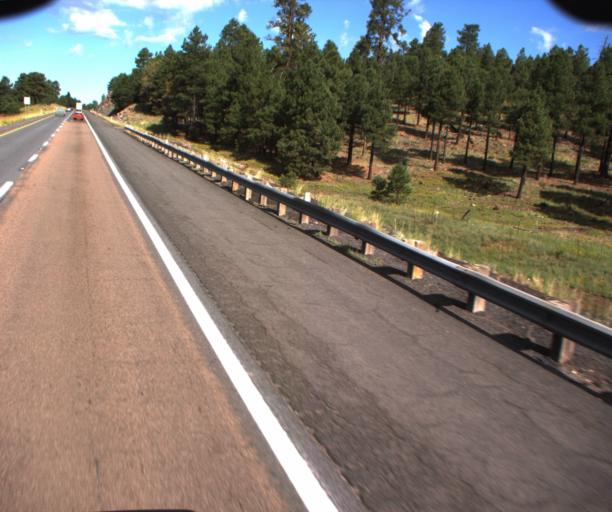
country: US
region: Arizona
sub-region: Coconino County
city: Flagstaff
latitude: 35.2019
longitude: -111.7605
